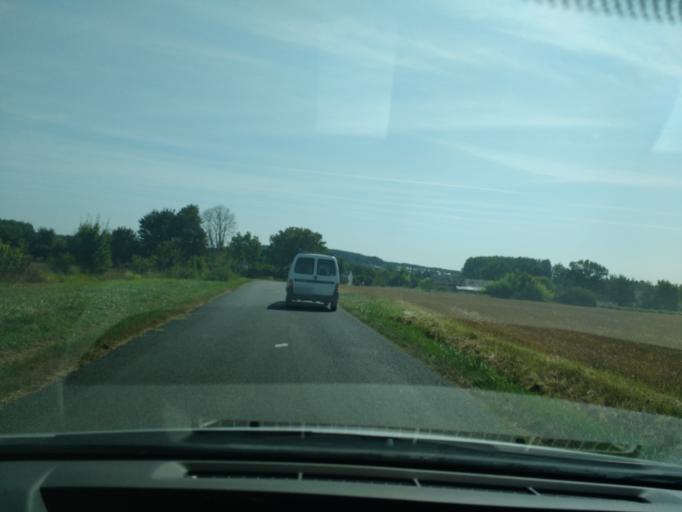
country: FR
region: Pays de la Loire
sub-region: Departement de Maine-et-Loire
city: Beaufort-en-Vallee
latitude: 47.4929
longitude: -0.2061
